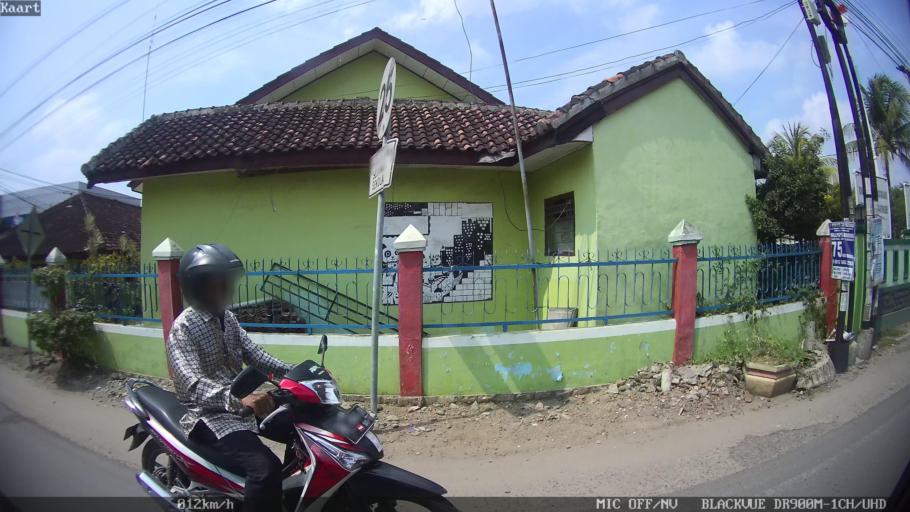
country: ID
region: Lampung
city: Pringsewu
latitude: -5.3550
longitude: 104.9731
